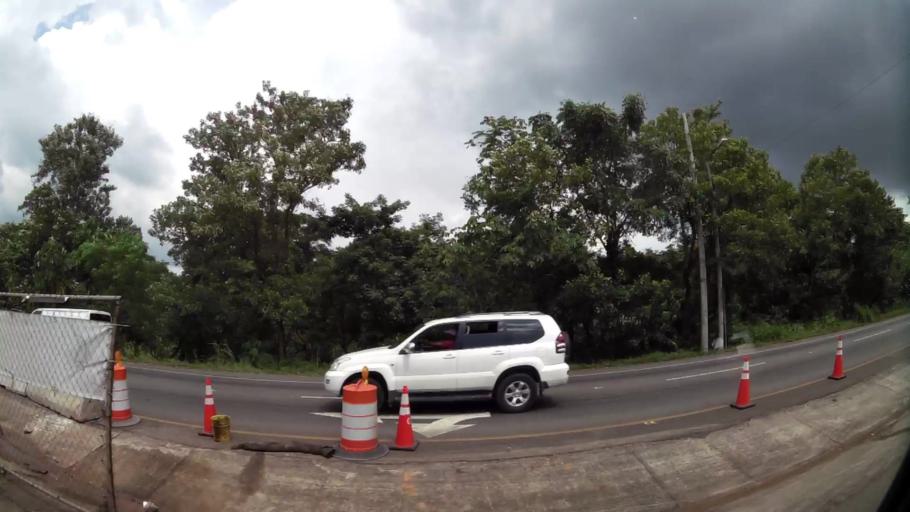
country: PA
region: Panama
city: Cabra Numero Uno
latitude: 9.1017
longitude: -79.3484
